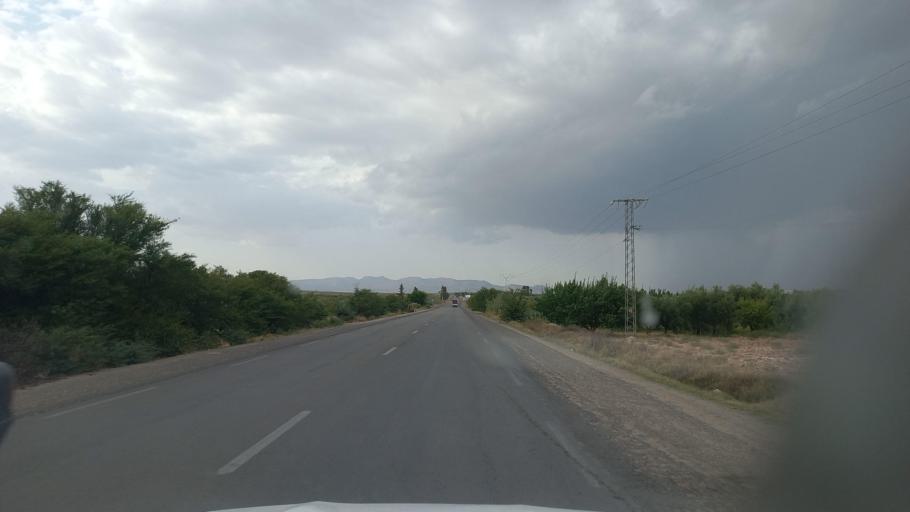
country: TN
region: Al Qasrayn
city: Sbiba
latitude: 35.3037
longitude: 9.0875
